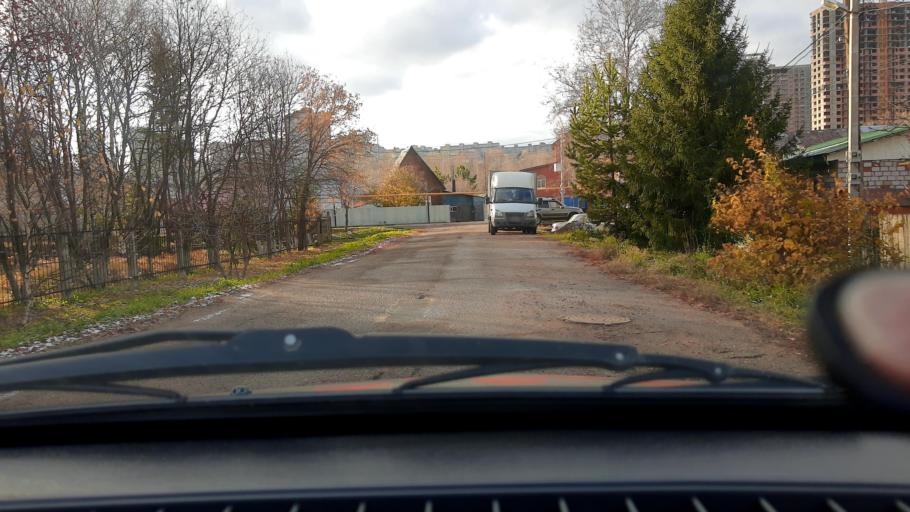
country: RU
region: Bashkortostan
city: Ufa
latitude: 54.7791
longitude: 56.0555
